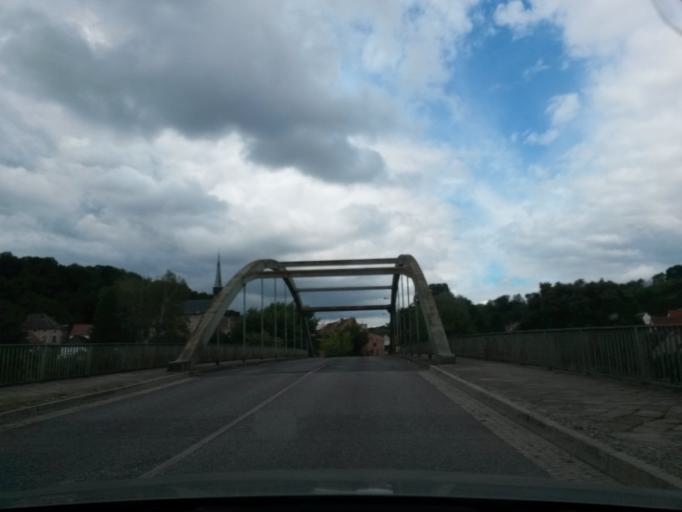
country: DE
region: Brandenburg
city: Oderberg
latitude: 52.8641
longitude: 14.0454
